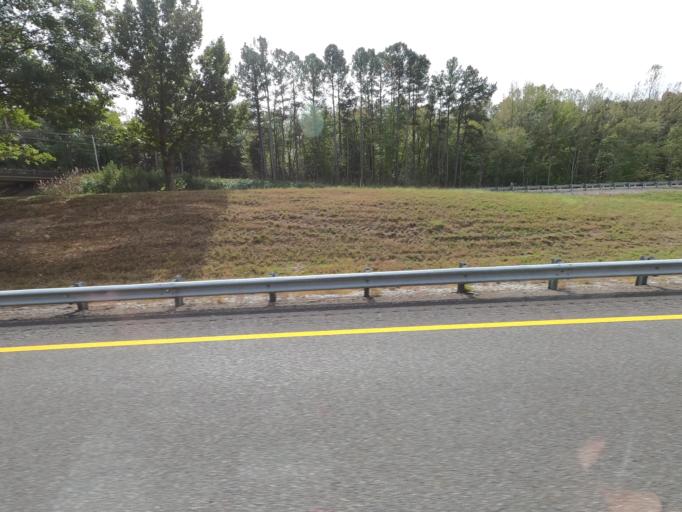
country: US
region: Tennessee
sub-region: Decatur County
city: Parsons
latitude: 35.8150
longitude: -88.2072
